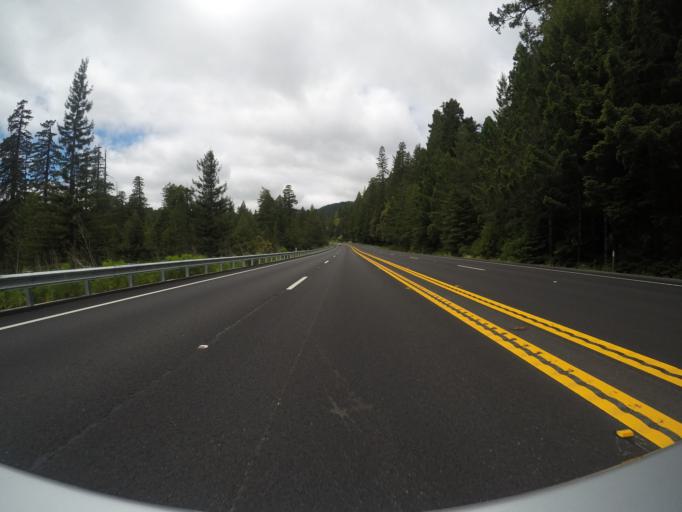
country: US
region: California
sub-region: Humboldt County
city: Redway
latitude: 40.3317
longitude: -123.9274
